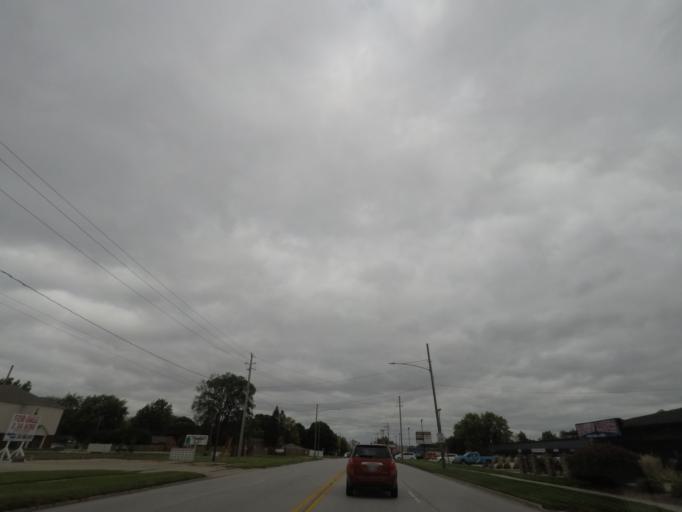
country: US
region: Iowa
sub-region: Polk County
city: Ankeny
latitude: 41.7235
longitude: -93.6004
